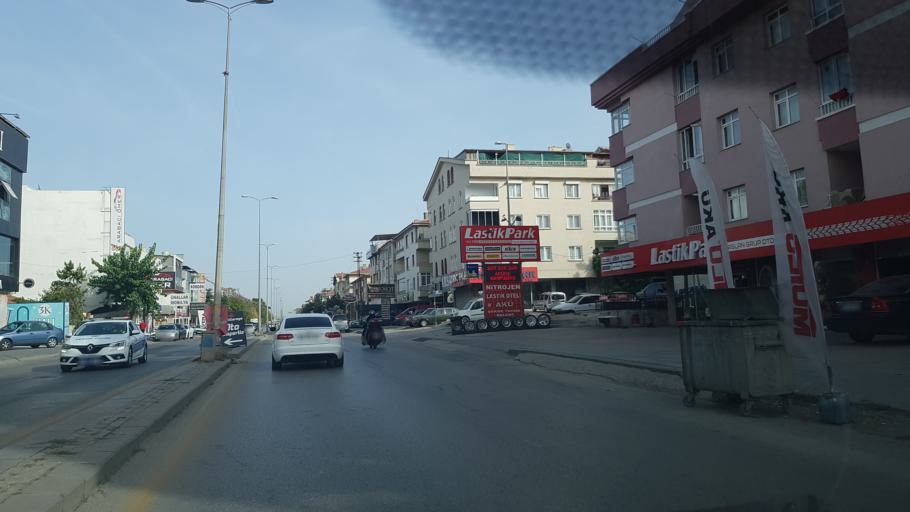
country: TR
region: Ankara
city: Etimesgut
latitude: 39.9500
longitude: 32.6553
